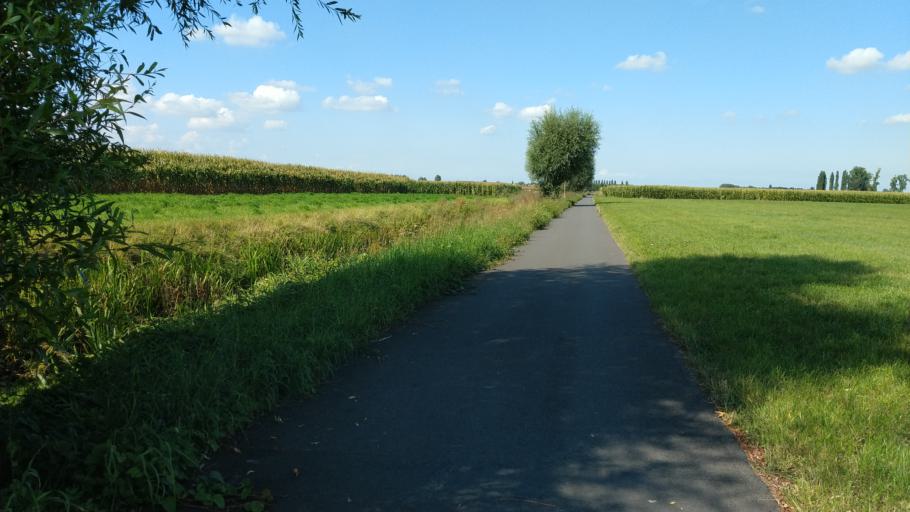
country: BE
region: Flanders
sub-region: Provincie Oost-Vlaanderen
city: Assenede
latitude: 51.2366
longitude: 3.7283
